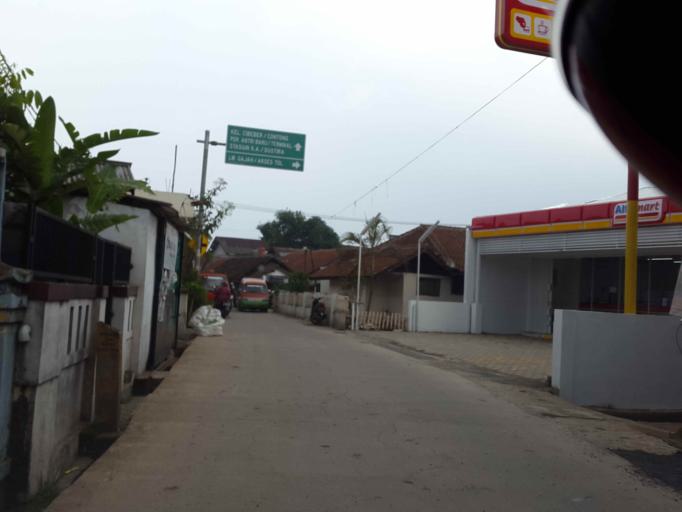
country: ID
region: West Java
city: Cimahi
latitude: -6.8975
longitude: 107.5190
